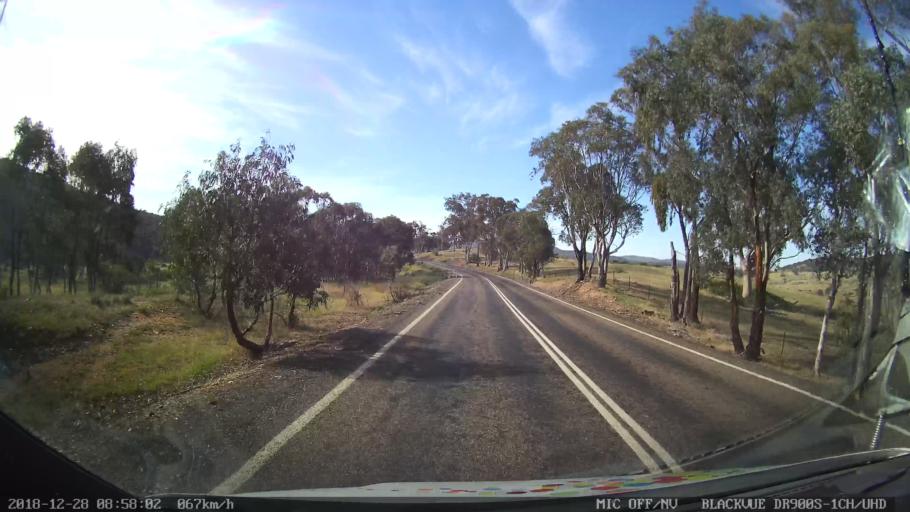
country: AU
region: New South Wales
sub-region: Upper Lachlan Shire
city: Crookwell
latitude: -34.1237
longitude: 149.3320
